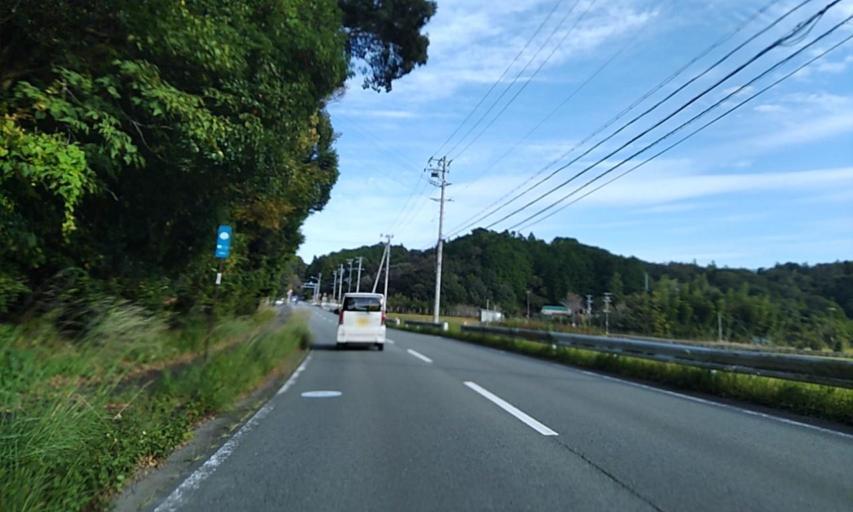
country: JP
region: Mie
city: Ise
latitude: 34.3450
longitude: 136.7183
